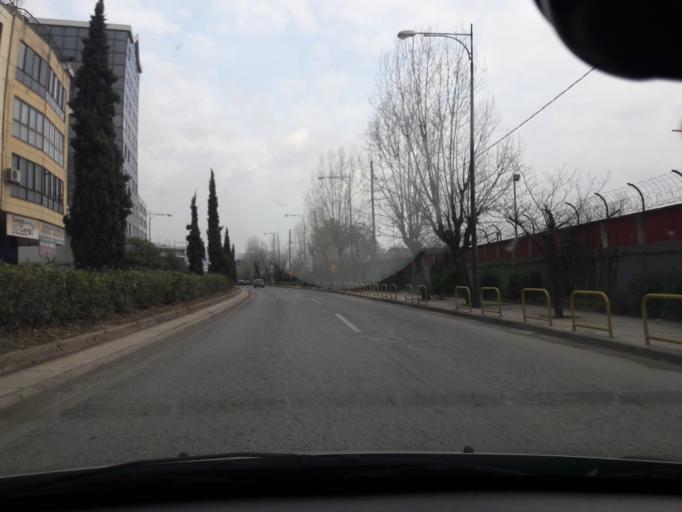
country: GR
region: Central Macedonia
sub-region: Nomos Thessalonikis
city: Thessaloniki
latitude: 40.6404
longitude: 22.9206
